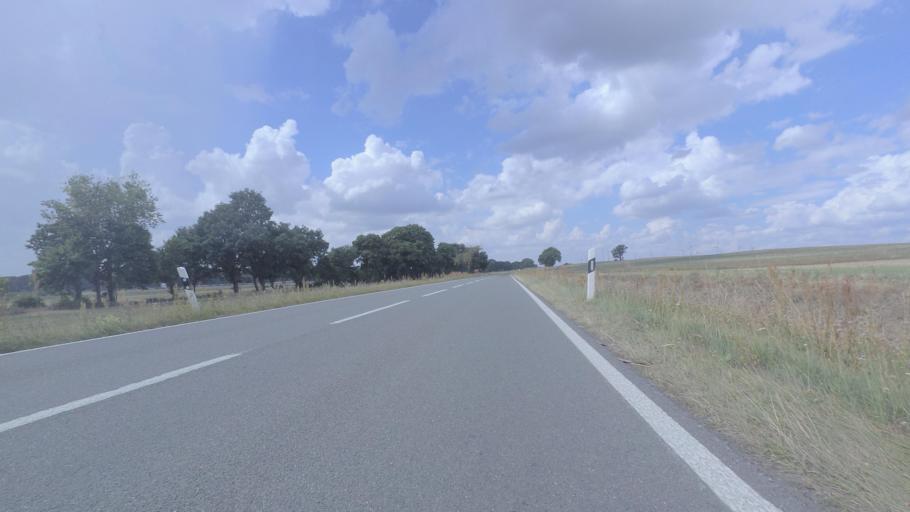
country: DE
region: Brandenburg
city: Wittstock
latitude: 53.1963
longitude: 12.4614
